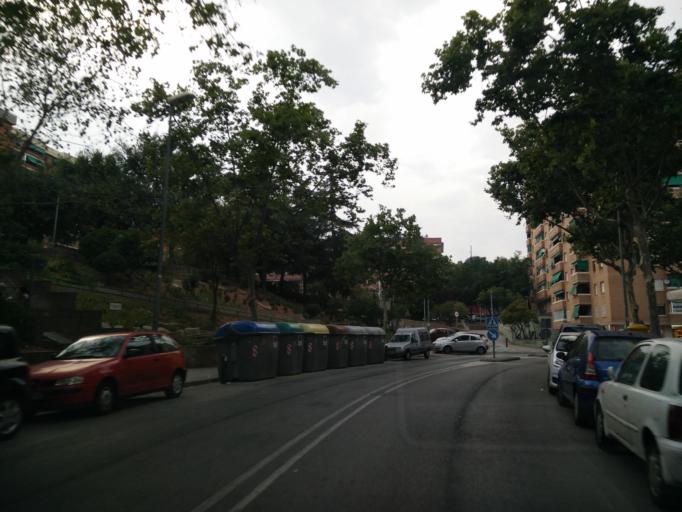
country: ES
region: Catalonia
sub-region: Provincia de Barcelona
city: Llefia
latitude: 41.4494
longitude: 2.2299
